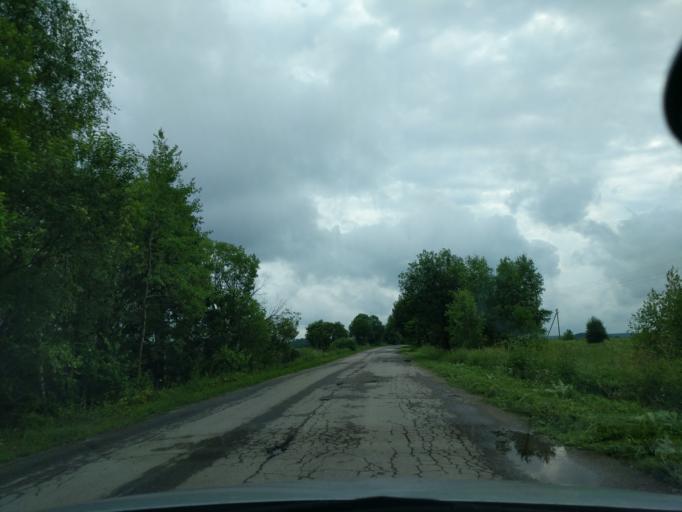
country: RU
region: Kaluga
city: Myatlevo
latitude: 54.7829
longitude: 35.7306
